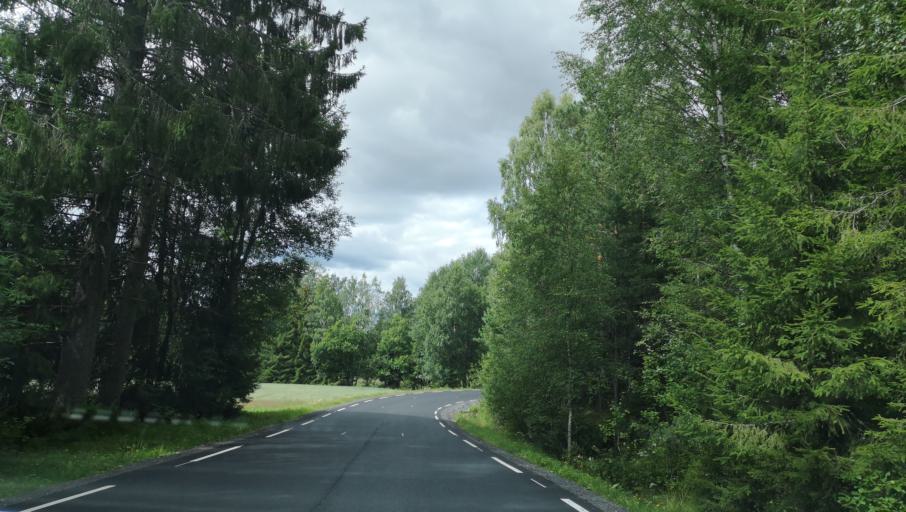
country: NO
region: Ostfold
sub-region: Hobol
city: Elvestad
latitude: 59.6825
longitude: 10.9381
